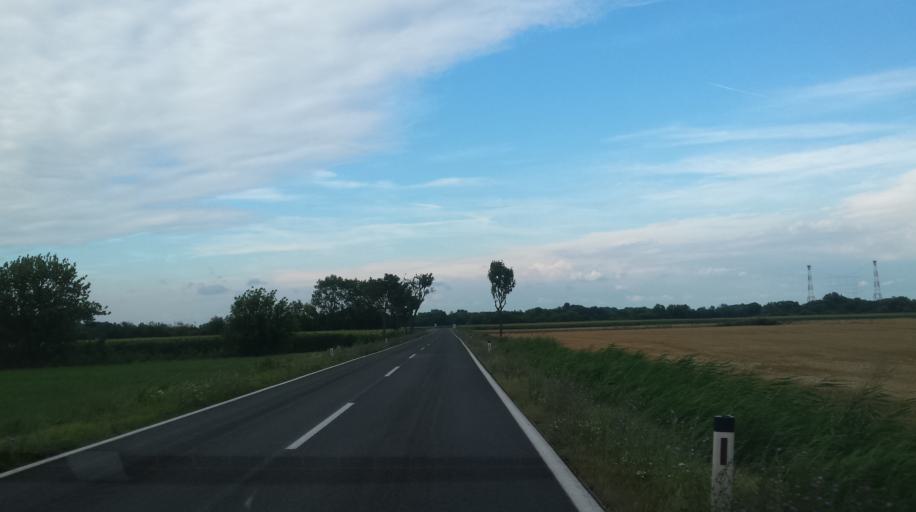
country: AT
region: Lower Austria
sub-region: Politischer Bezirk Wien-Umgebung
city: Moosbrunn
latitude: 48.0044
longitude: 16.4469
